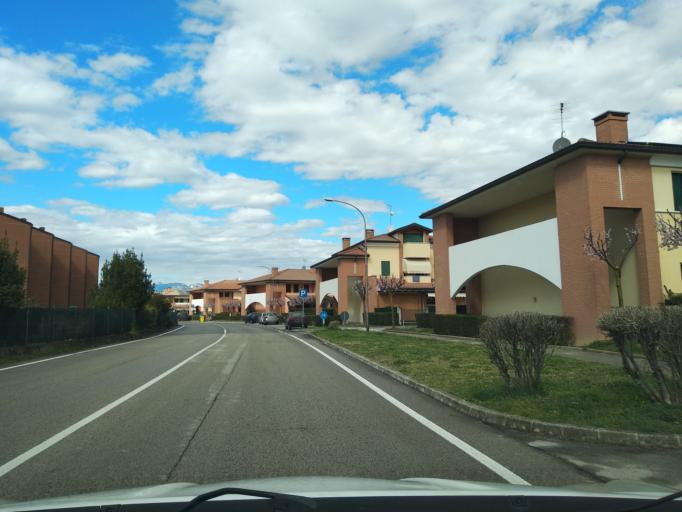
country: IT
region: Veneto
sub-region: Provincia di Vicenza
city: Monticello Conte Otto
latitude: 45.6032
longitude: 11.5773
